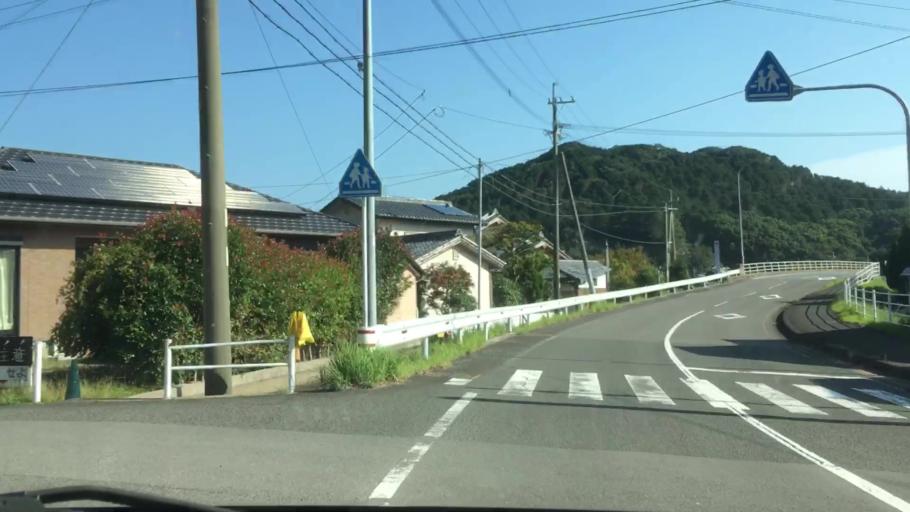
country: JP
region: Nagasaki
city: Sasebo
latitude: 32.9936
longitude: 129.6513
